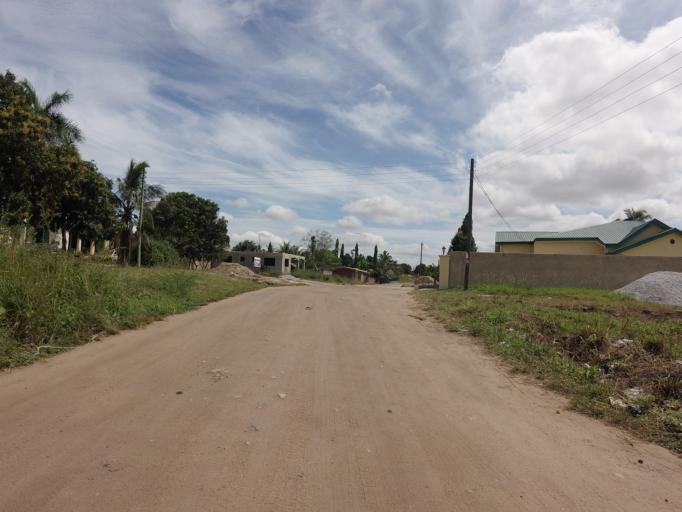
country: GH
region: Central
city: Kasoa
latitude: 5.5215
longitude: -0.4519
